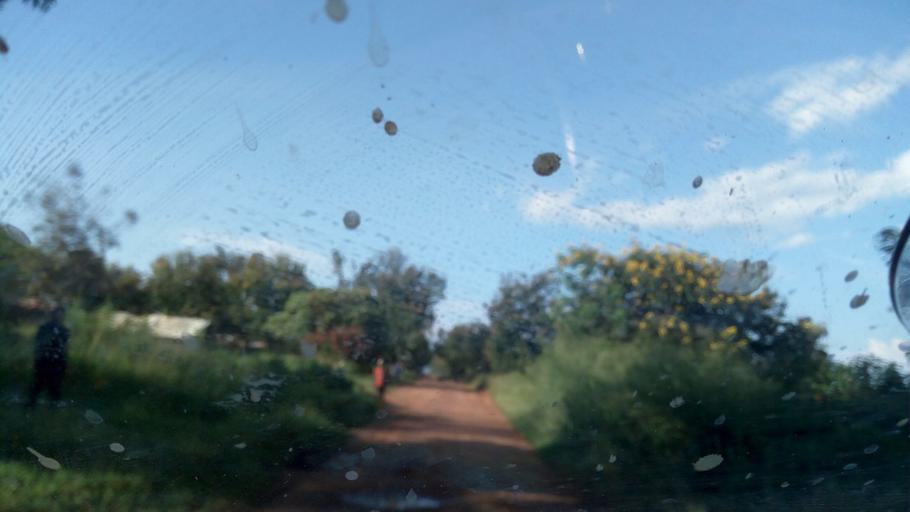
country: BI
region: Bururi
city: Rumonge
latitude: -4.2536
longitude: 28.9871
